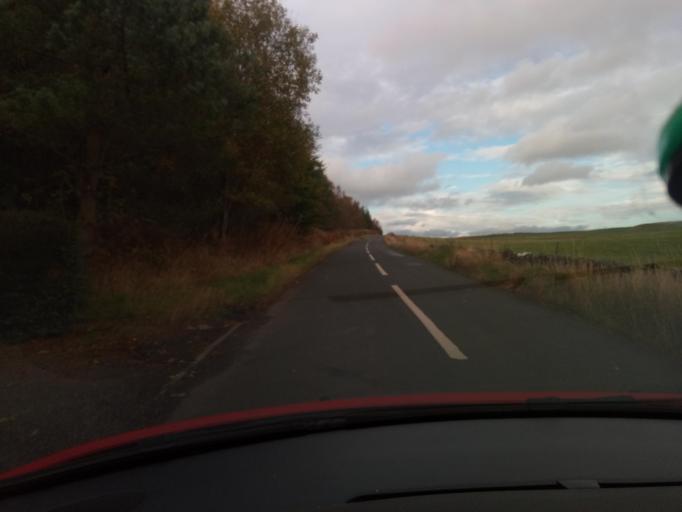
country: GB
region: Scotland
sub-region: South Lanarkshire
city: Carnwath
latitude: 55.7134
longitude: -3.5972
